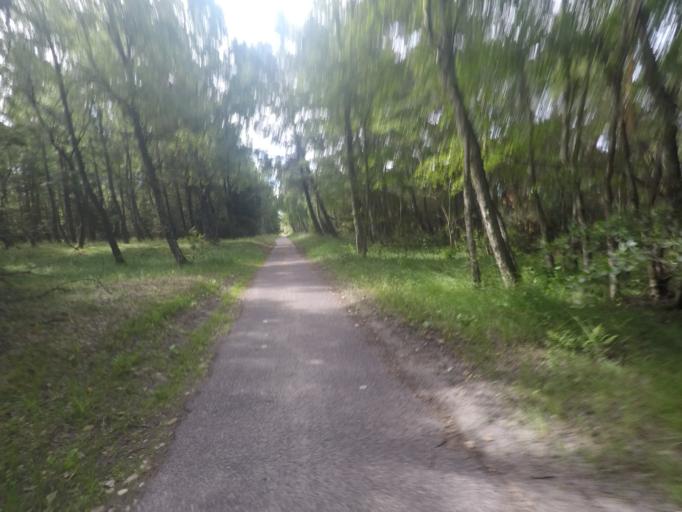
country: LT
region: Klaipedos apskritis
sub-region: Klaipeda
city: Klaipeda
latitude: 55.6500
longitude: 21.1081
